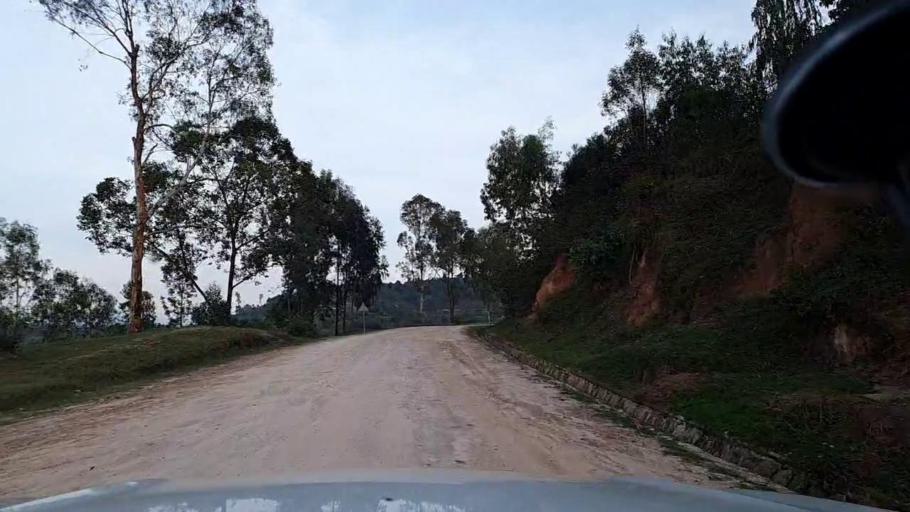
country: RW
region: Southern Province
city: Nyanza
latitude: -2.2231
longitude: 29.6491
